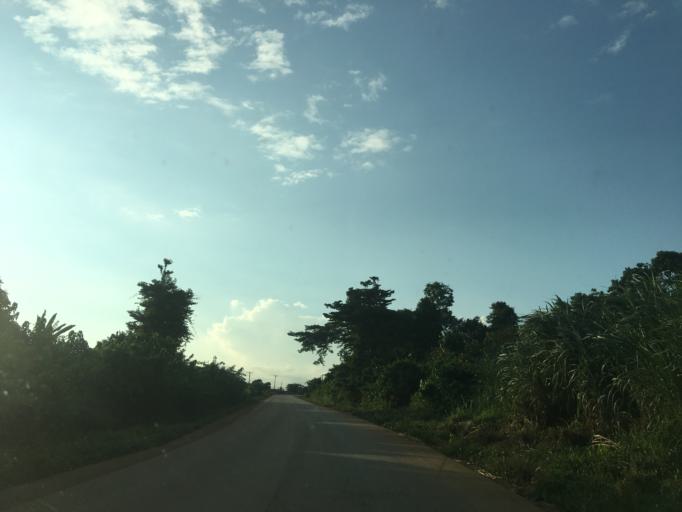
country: GH
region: Western
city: Bibiani
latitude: 6.5652
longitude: -2.3702
